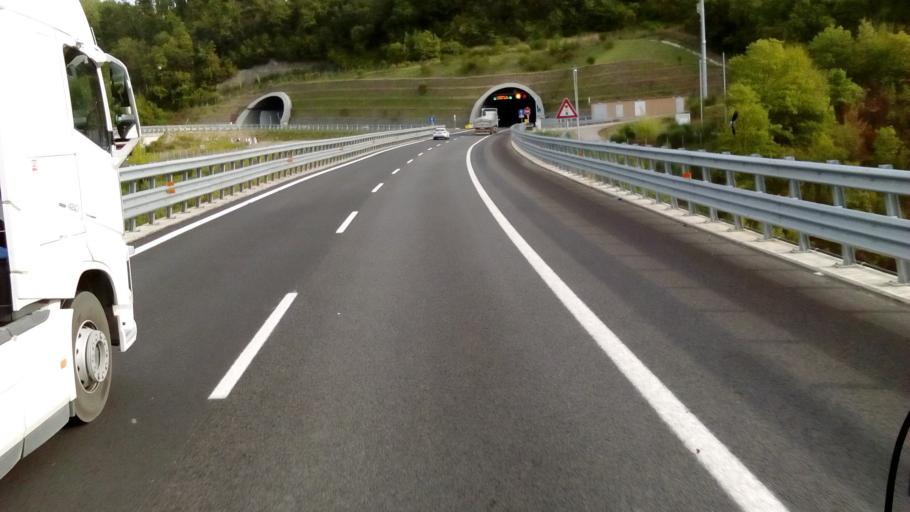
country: IT
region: Tuscany
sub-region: Province of Florence
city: Barberino di Mugello
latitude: 44.0371
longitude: 11.2271
